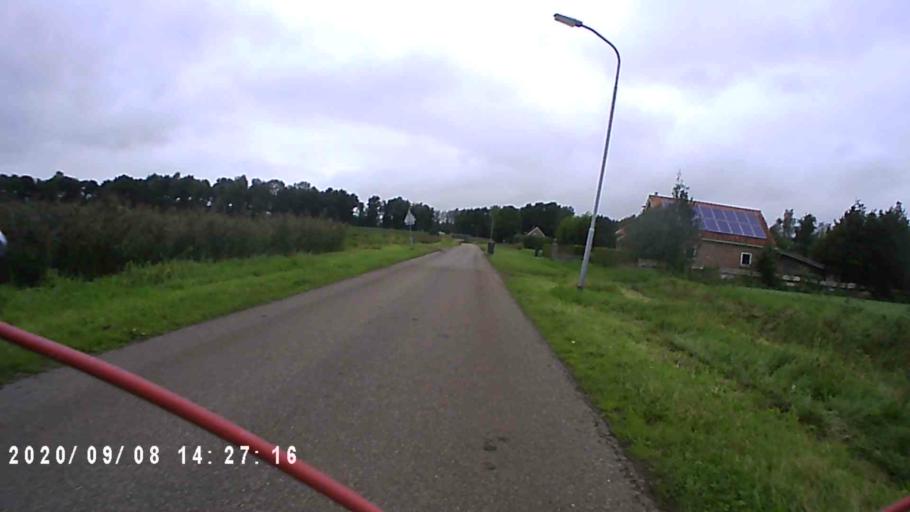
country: NL
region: Groningen
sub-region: Gemeente Slochteren
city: Slochteren
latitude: 53.2229
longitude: 6.8179
